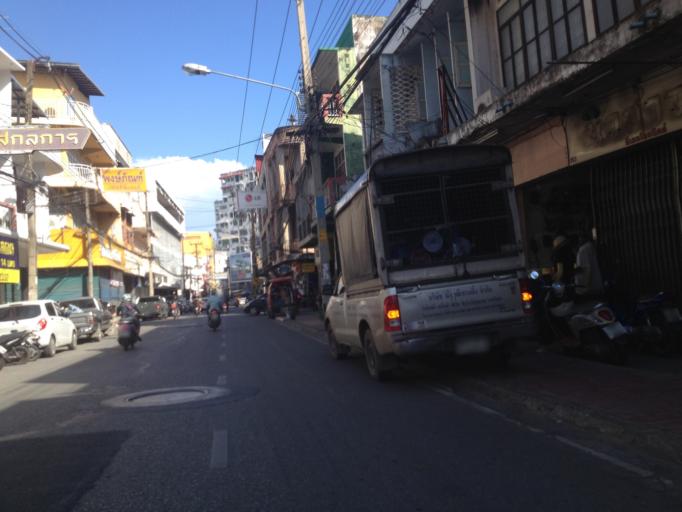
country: TH
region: Chiang Mai
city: Chiang Mai
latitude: 18.7902
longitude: 98.9950
